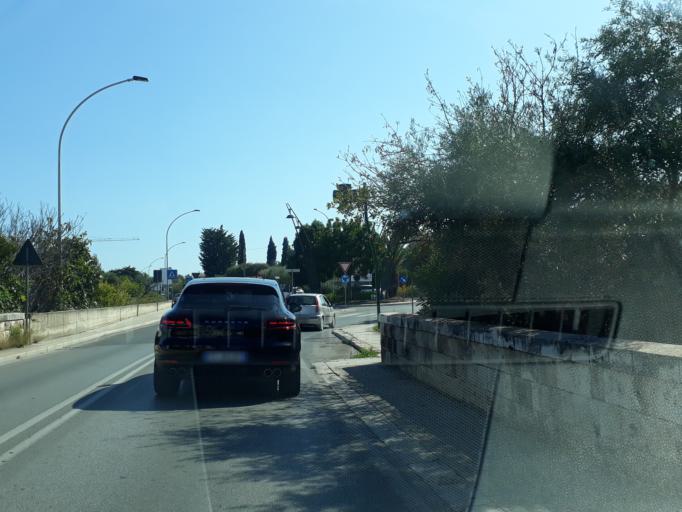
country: IT
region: Apulia
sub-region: Provincia di Bari
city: Monopoli
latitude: 40.9466
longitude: 17.2935
